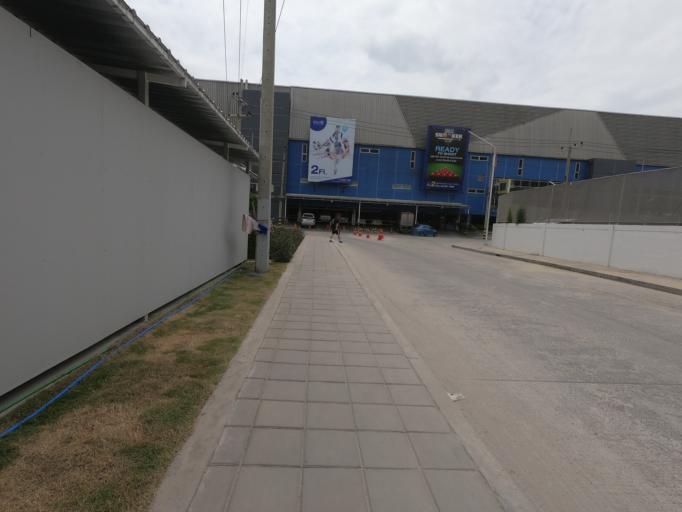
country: TH
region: Bangkok
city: Sai Mai
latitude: 13.9429
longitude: 100.6515
